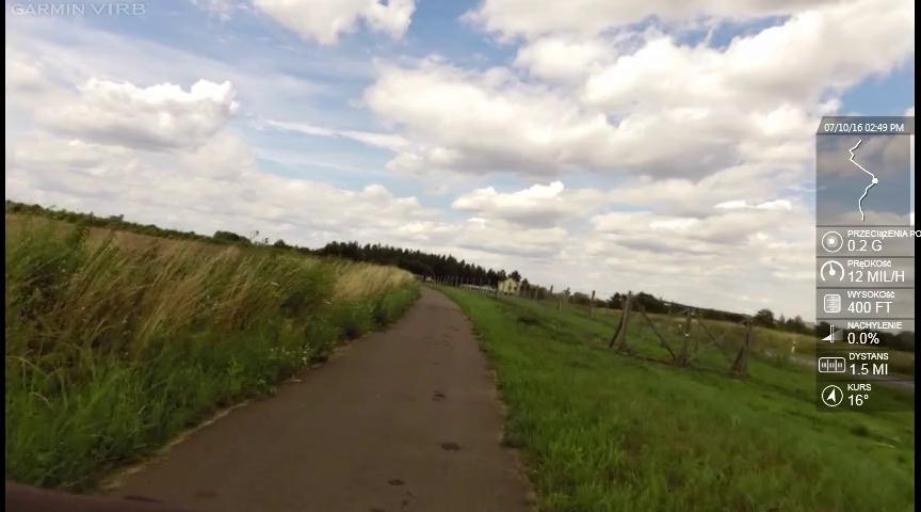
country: PL
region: West Pomeranian Voivodeship
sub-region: Powiat gryfinski
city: Banie
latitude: 53.0954
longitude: 14.6502
